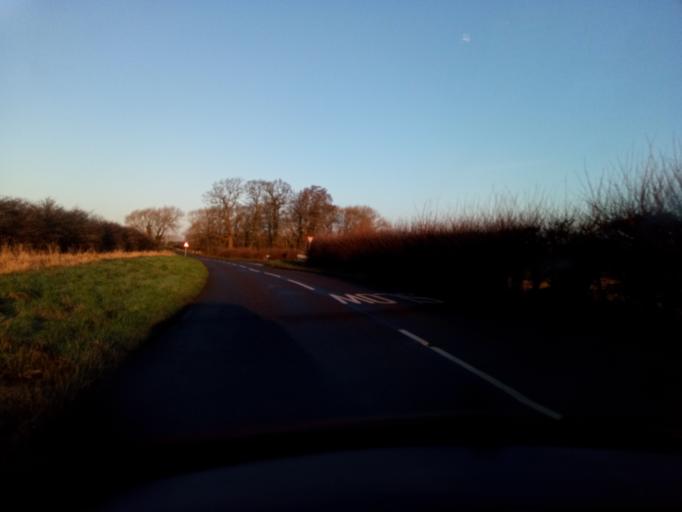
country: GB
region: England
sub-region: Leicestershire
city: Quorndon
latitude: 52.7765
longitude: -1.1688
